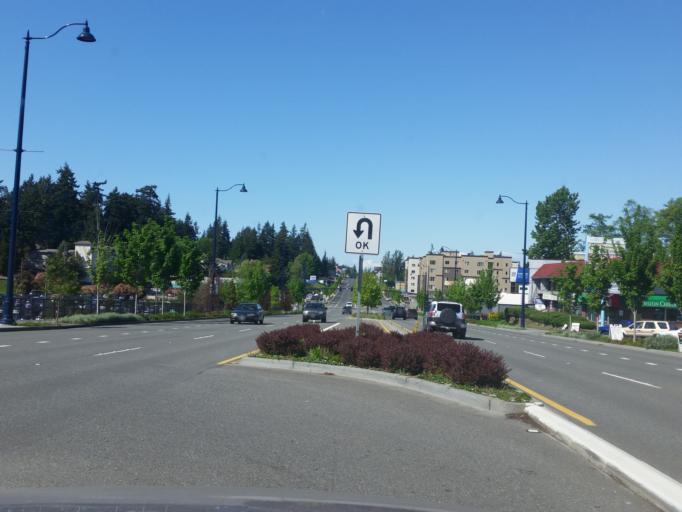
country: US
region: Washington
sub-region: King County
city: Shoreline
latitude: 47.7656
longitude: -122.3459
